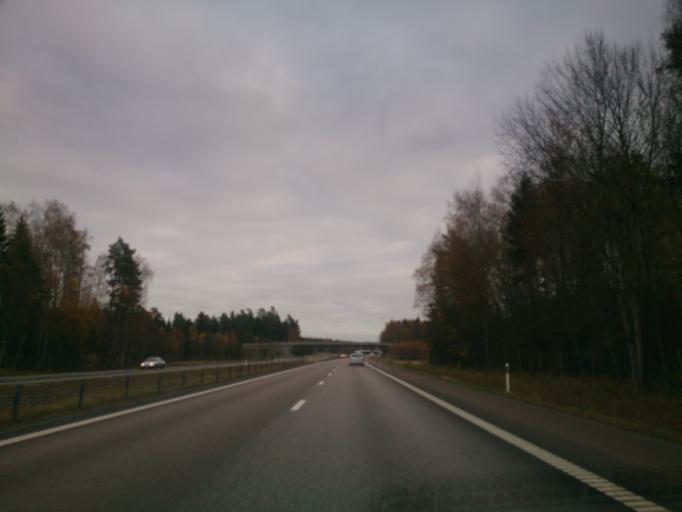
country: SE
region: Soedermanland
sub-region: Nykopings Kommun
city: Svalsta
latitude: 58.7510
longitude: 16.9080
